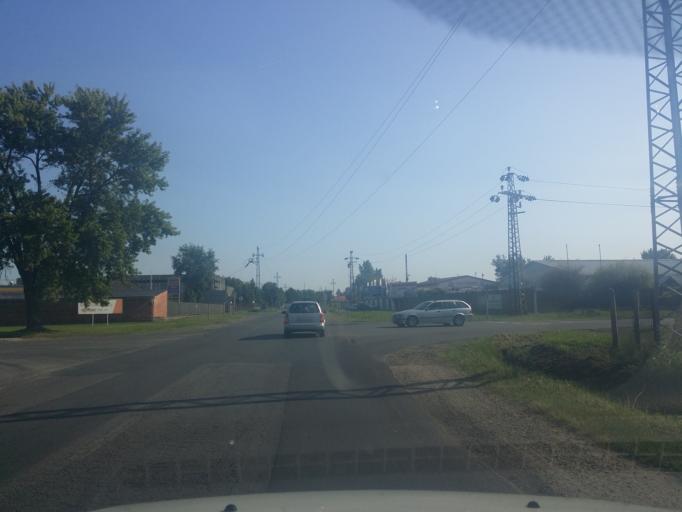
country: HU
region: Bacs-Kiskun
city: Baja
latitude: 46.1717
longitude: 18.9764
